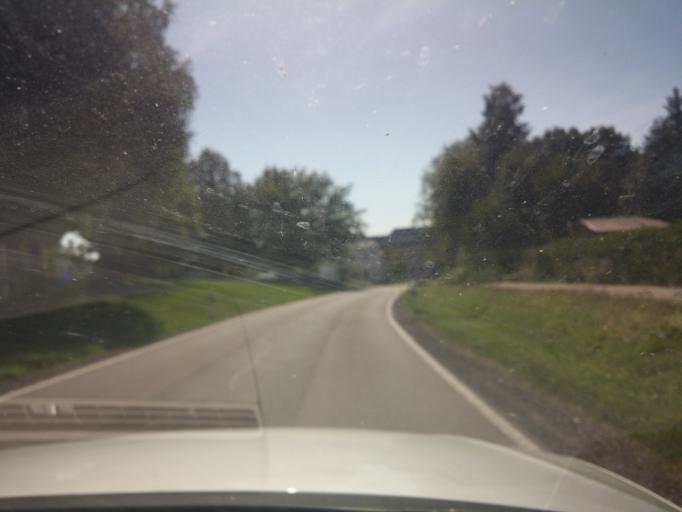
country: DE
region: Baden-Wuerttemberg
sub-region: Tuebingen Region
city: Herbertingen
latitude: 48.0604
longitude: 9.4420
